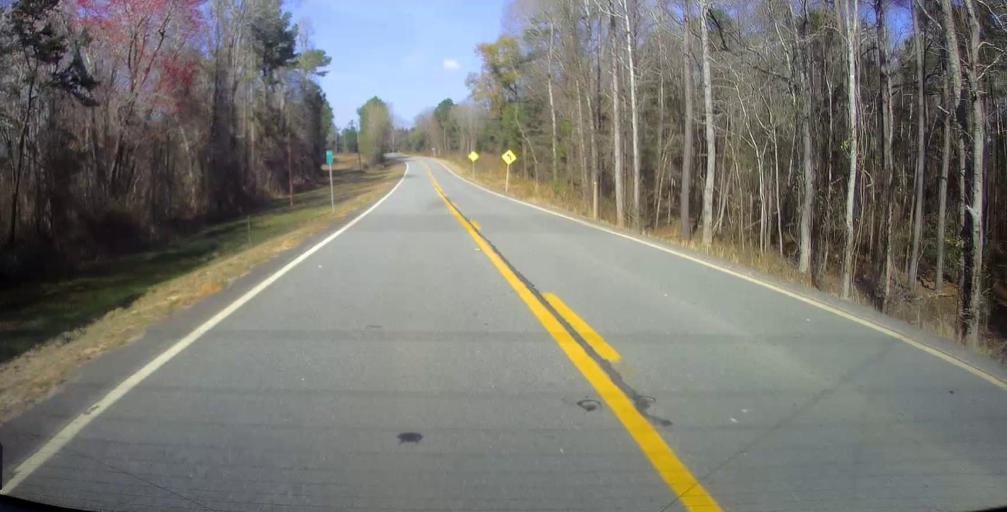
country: US
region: Georgia
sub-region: Twiggs County
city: Jeffersonville
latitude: 32.7822
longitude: -83.3306
